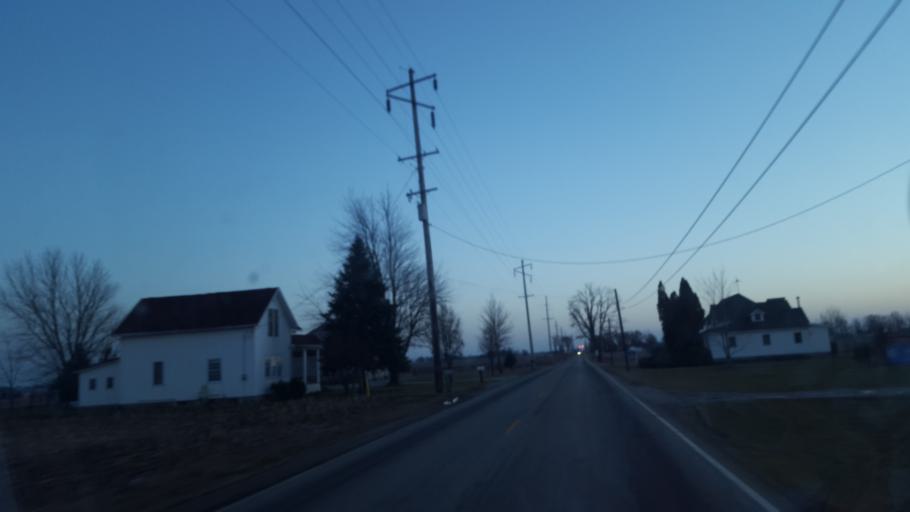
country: US
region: Indiana
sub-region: Elkhart County
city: Nappanee
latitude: 41.3671
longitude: -86.0007
